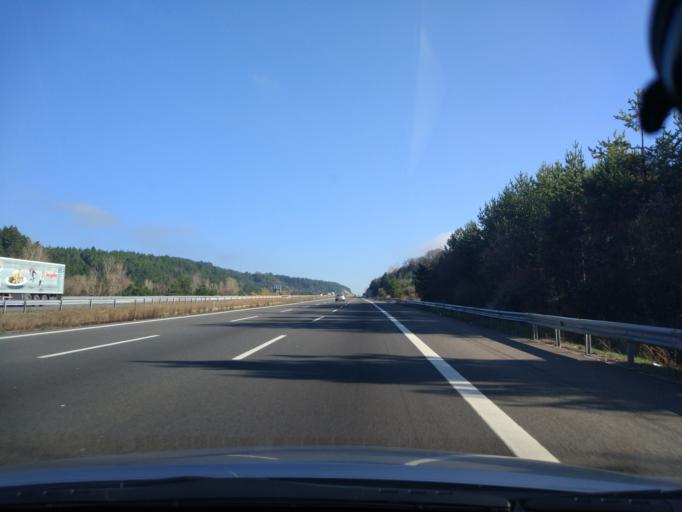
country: TR
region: Bolu
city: Yenicaga
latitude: 40.7447
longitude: 31.8733
